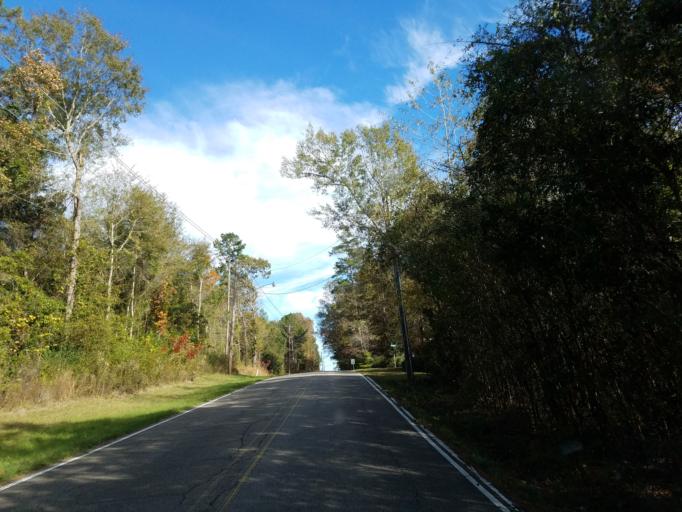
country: US
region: Mississippi
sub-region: Lamar County
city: Arnold Line
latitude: 31.3467
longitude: -89.3482
